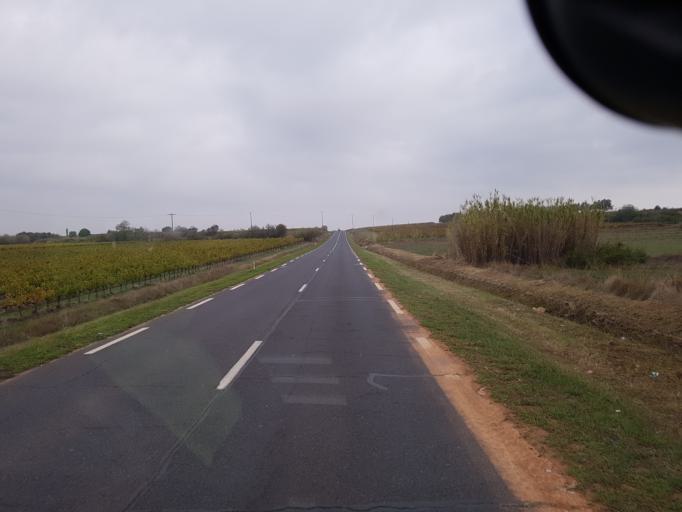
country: FR
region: Languedoc-Roussillon
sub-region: Departement de l'Herault
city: Marseillan
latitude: 43.3694
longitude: 3.5320
